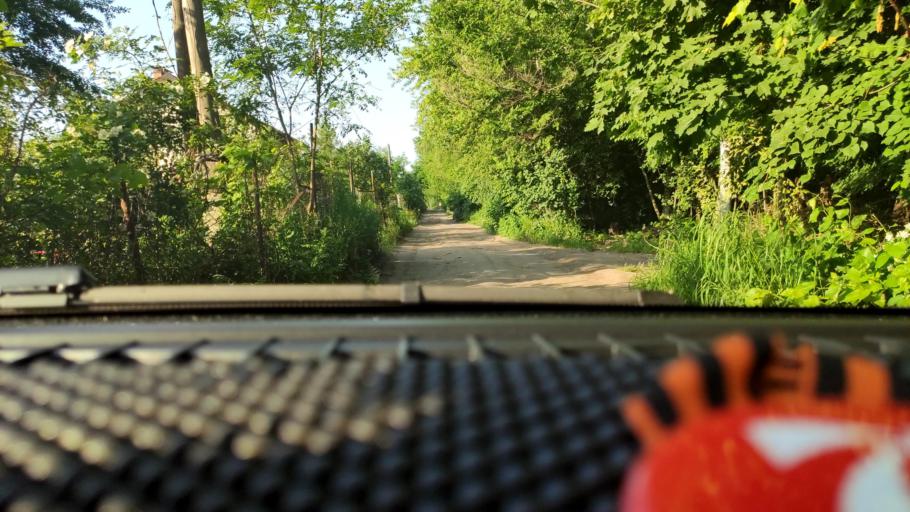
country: RU
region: Voronezj
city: Maslovka
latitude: 51.5924
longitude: 39.1691
